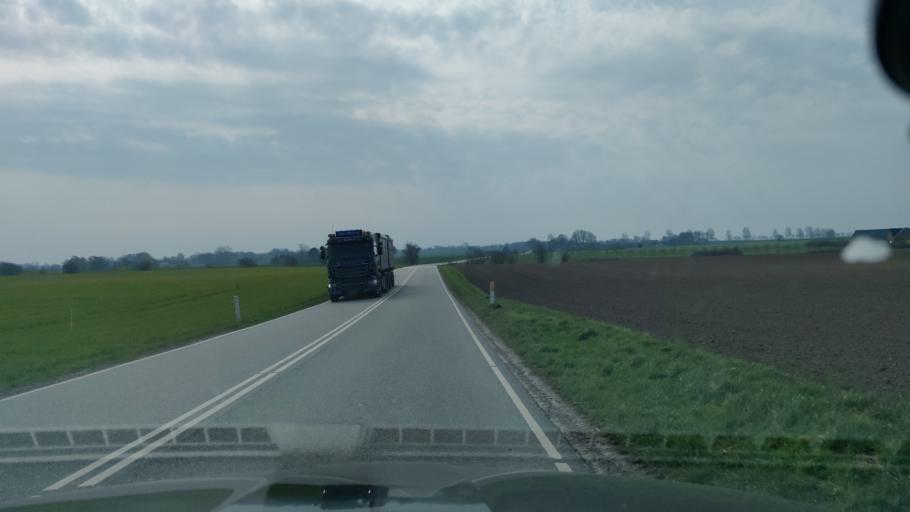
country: DK
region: South Denmark
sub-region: Nordfyns Kommune
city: Sonderso
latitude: 55.5060
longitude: 10.2501
